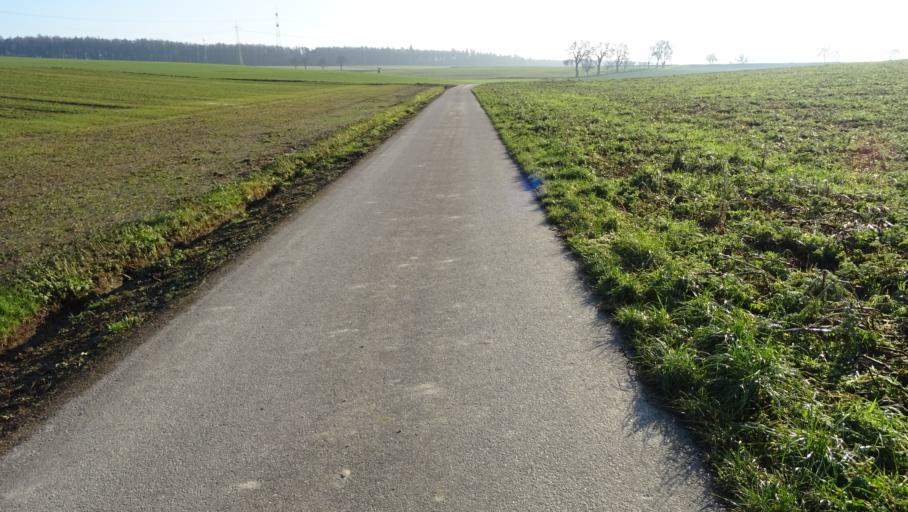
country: DE
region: Baden-Wuerttemberg
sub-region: Karlsruhe Region
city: Mosbach
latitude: 49.3480
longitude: 9.1882
